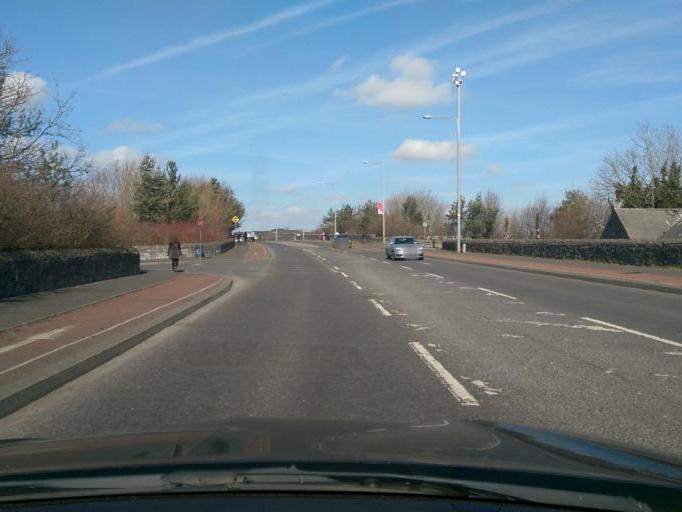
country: IE
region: Leinster
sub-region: Kildare
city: Maynooth
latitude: 53.3773
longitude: -6.5875
